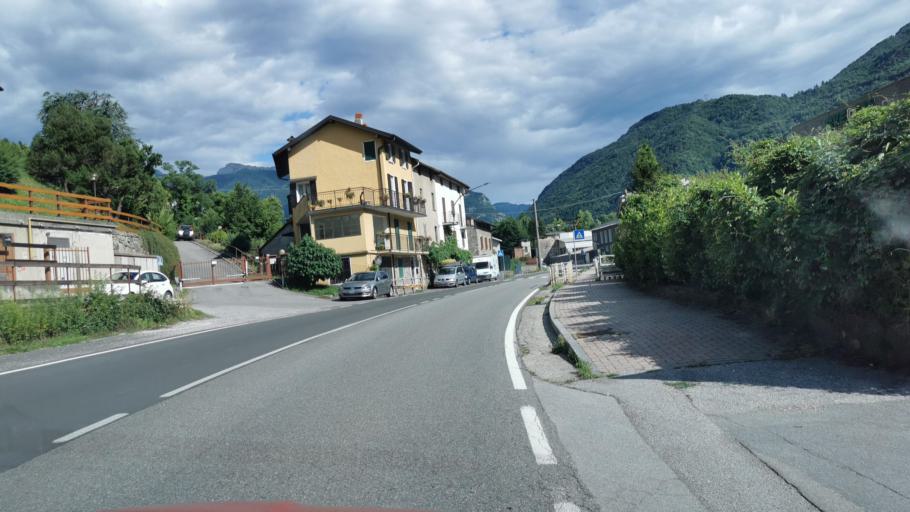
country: IT
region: Lombardy
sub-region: Provincia di Lecco
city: Primaluna
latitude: 45.9916
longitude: 9.4121
